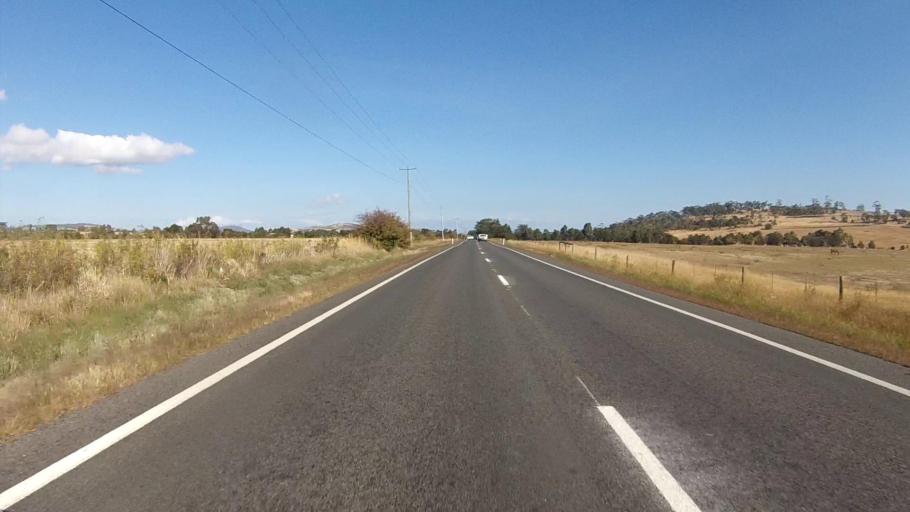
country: AU
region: Tasmania
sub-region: Sorell
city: Sorell
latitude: -42.7196
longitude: 147.5200
